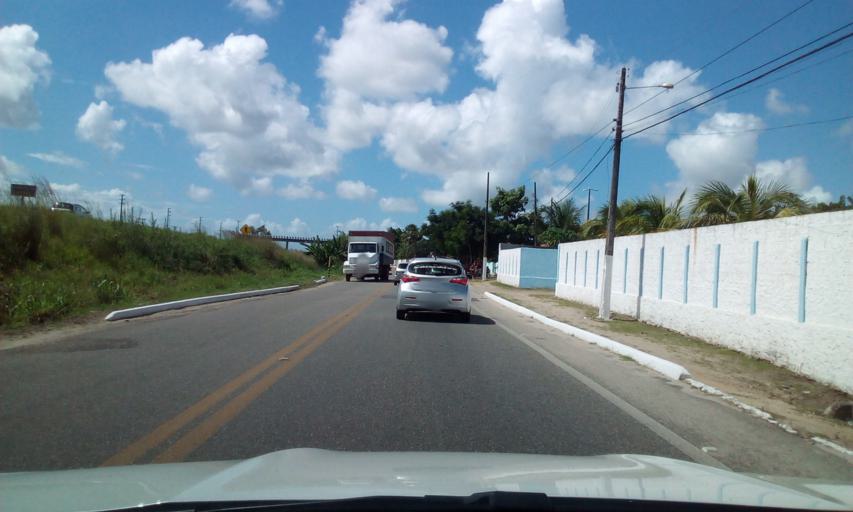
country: BR
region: Paraiba
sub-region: Bayeux
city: Bayeux
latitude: -7.1296
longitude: -34.9534
